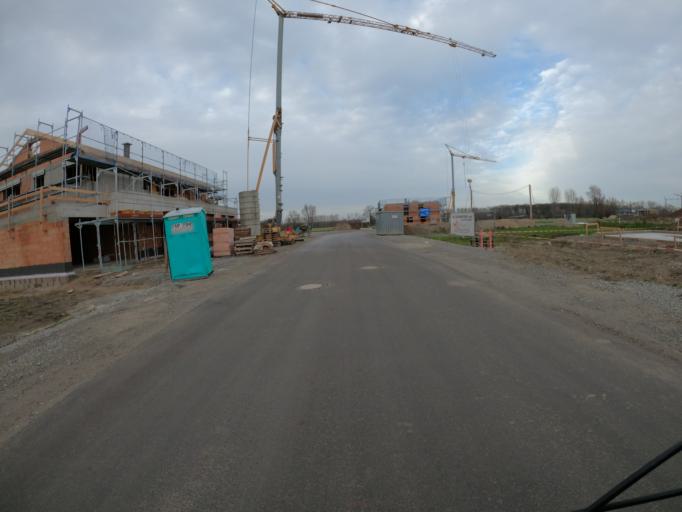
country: DE
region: North Rhine-Westphalia
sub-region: Regierungsbezirk Arnsberg
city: Lippstadt
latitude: 51.6854
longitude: 8.3292
